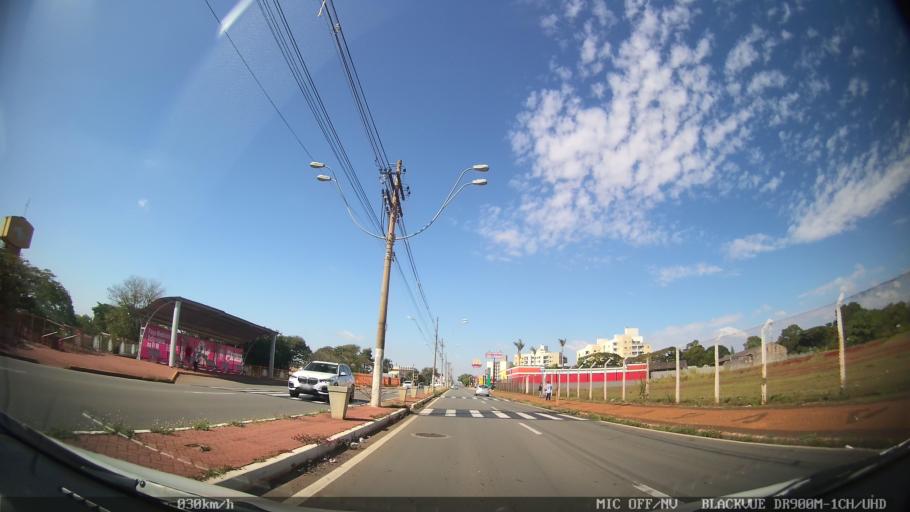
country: BR
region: Sao Paulo
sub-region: Americana
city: Americana
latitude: -22.7360
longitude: -47.3156
